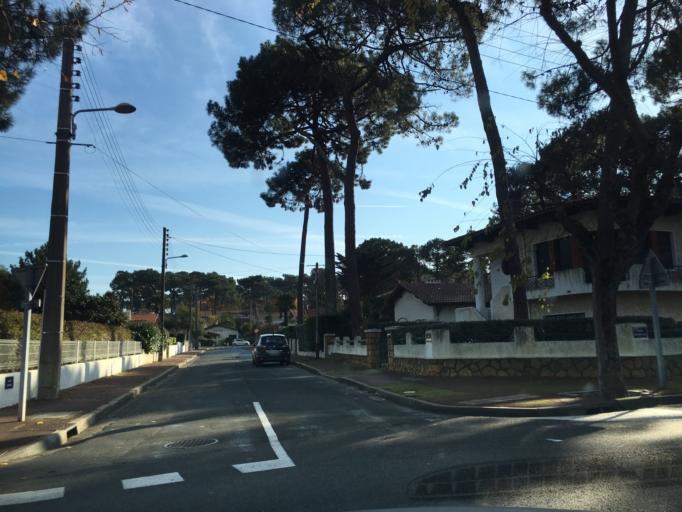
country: FR
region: Aquitaine
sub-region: Departement de la Gironde
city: Arcachon
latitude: 44.6514
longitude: -1.1844
